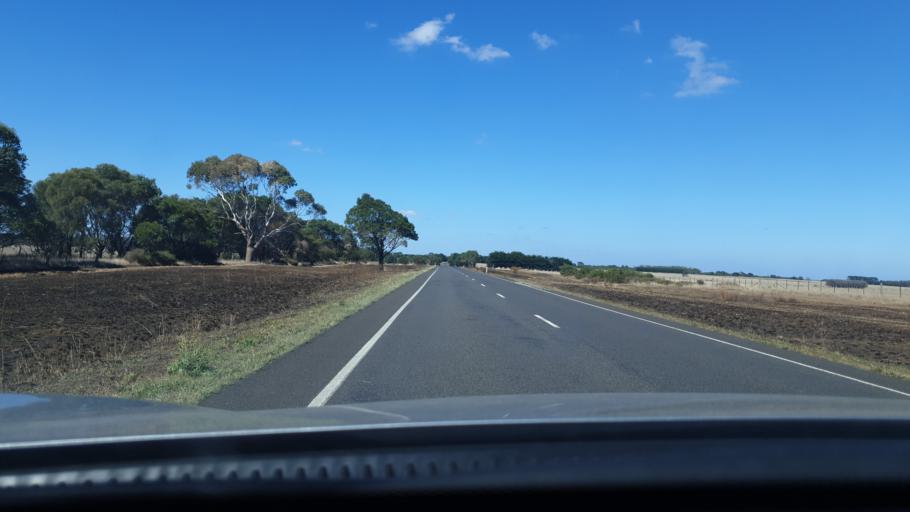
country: AU
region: Victoria
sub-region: Warrnambool
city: Warrnambool
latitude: -38.1732
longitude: 142.4094
